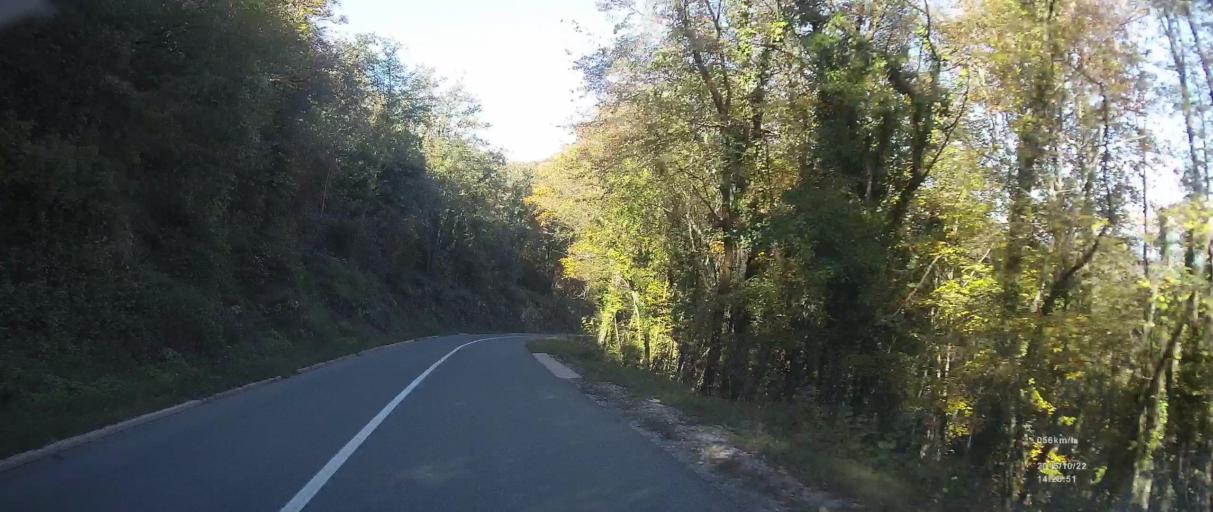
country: HR
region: Istarska
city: Lovran
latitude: 45.3274
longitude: 14.2478
